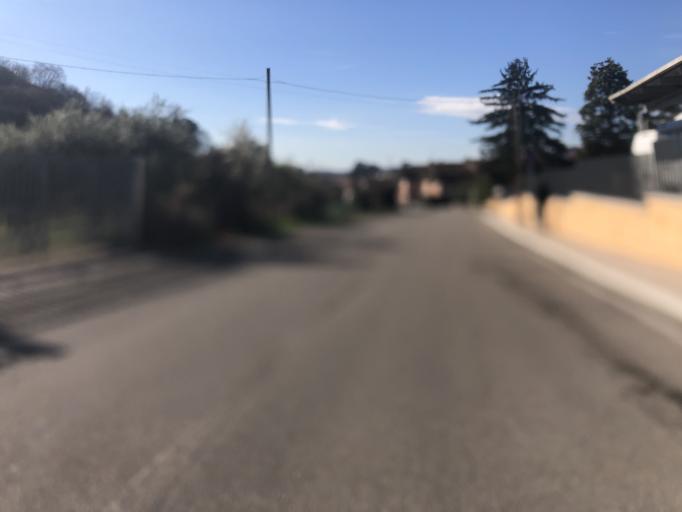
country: IT
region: Veneto
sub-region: Provincia di Verona
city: Sant'Ambrogio di Valpollicella
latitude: 45.5155
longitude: 10.8353
